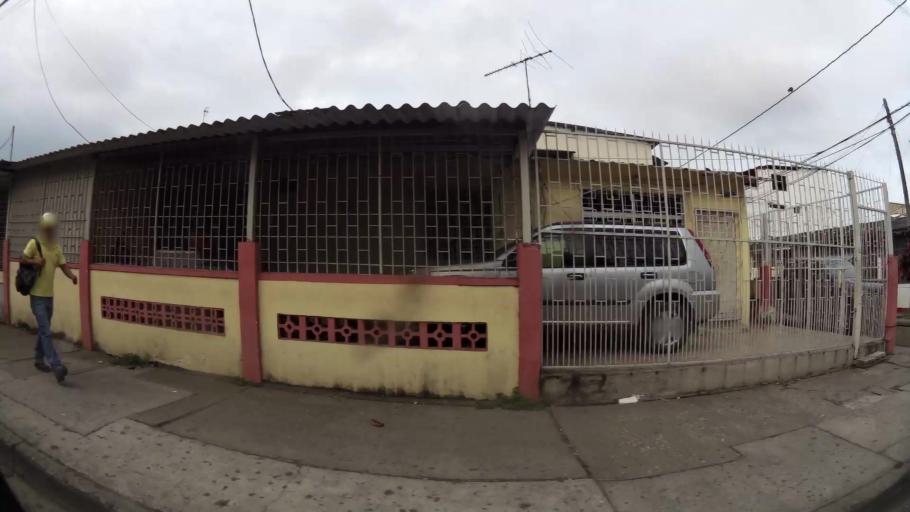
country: EC
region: Guayas
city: Eloy Alfaro
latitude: -2.1708
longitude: -79.8811
